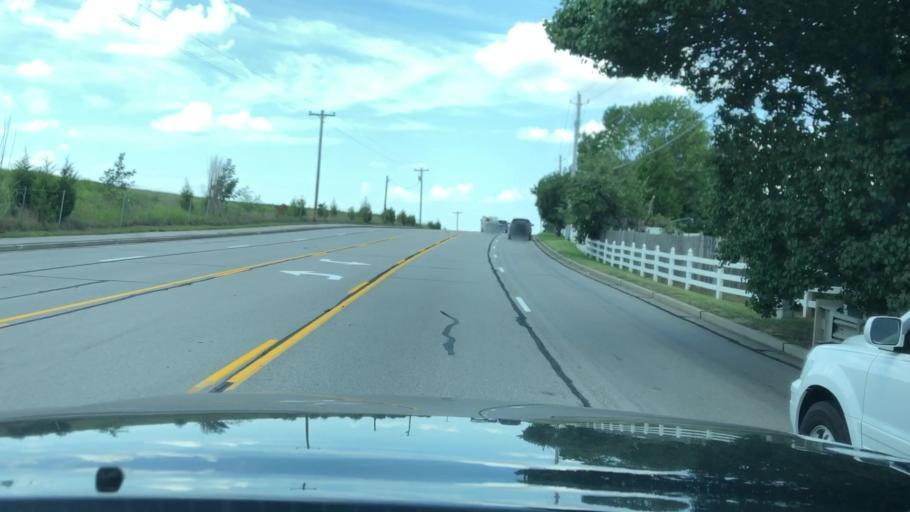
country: US
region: Missouri
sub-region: Saint Charles County
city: O'Fallon
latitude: 38.7898
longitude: -90.6803
